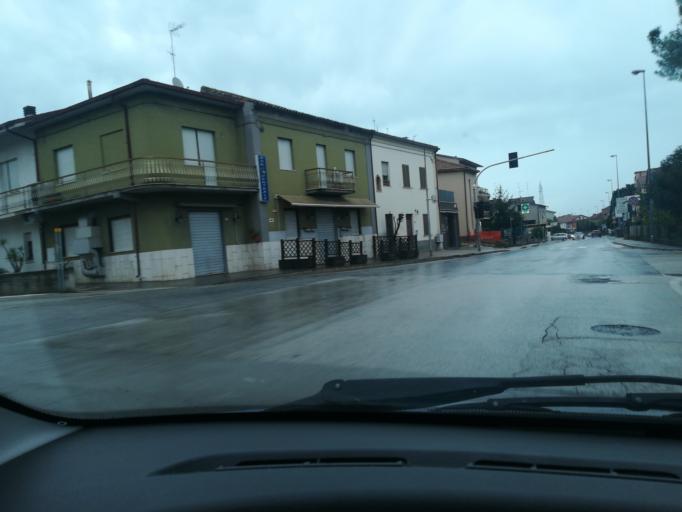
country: IT
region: The Marches
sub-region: Provincia di Macerata
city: Santa Maria Apparente
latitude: 43.2971
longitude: 13.6914
